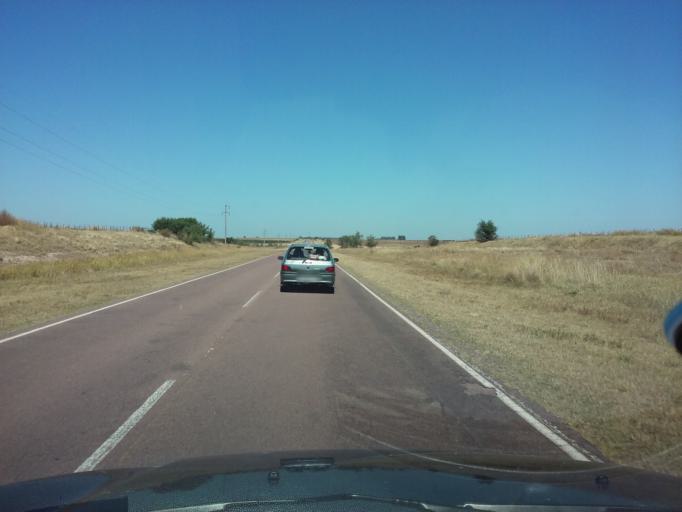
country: AR
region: La Pampa
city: Colonia Baron
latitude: -36.2054
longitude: -63.9424
